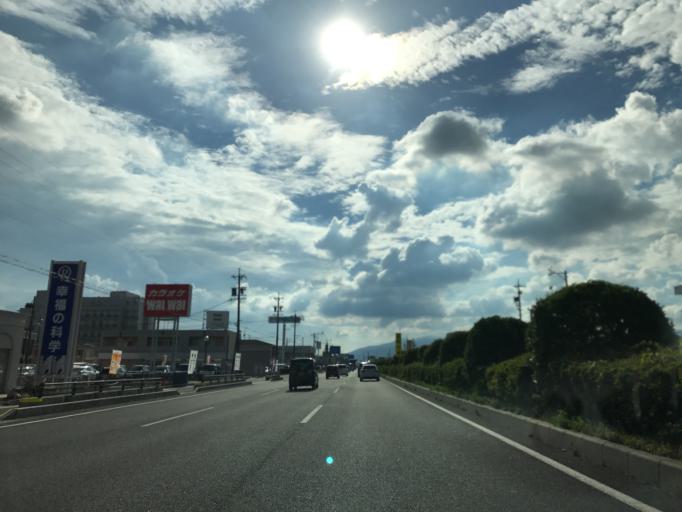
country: JP
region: Gifu
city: Ogaki
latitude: 35.3785
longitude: 136.6111
